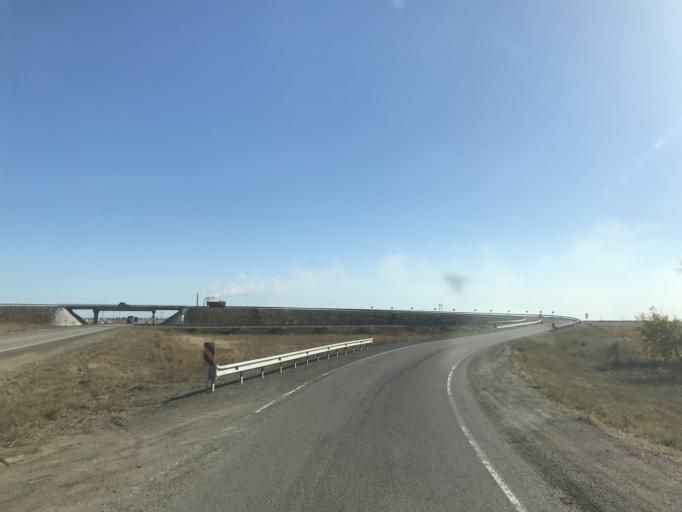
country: KZ
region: Pavlodar
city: Leninskiy
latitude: 52.1551
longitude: 76.8184
